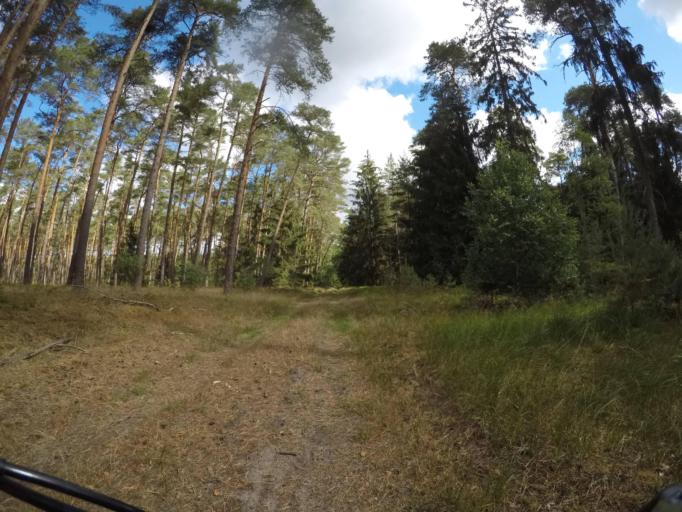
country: DE
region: Lower Saxony
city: Hitzacker
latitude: 53.2311
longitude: 11.0212
